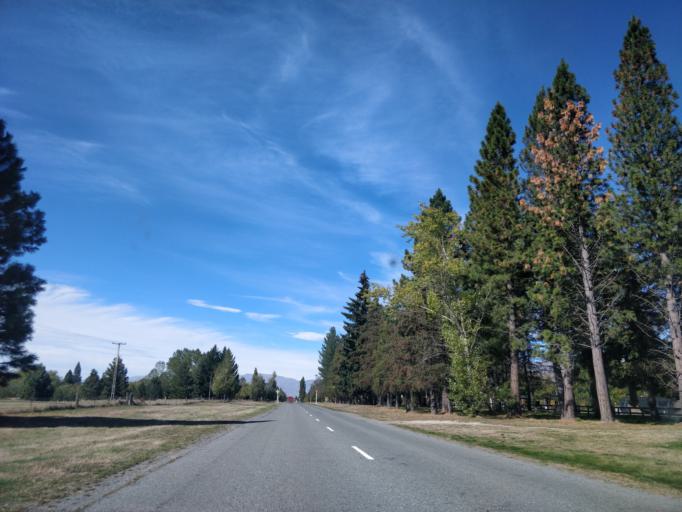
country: NZ
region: Canterbury
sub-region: Timaru District
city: Pleasant Point
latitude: -44.2510
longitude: 170.0997
